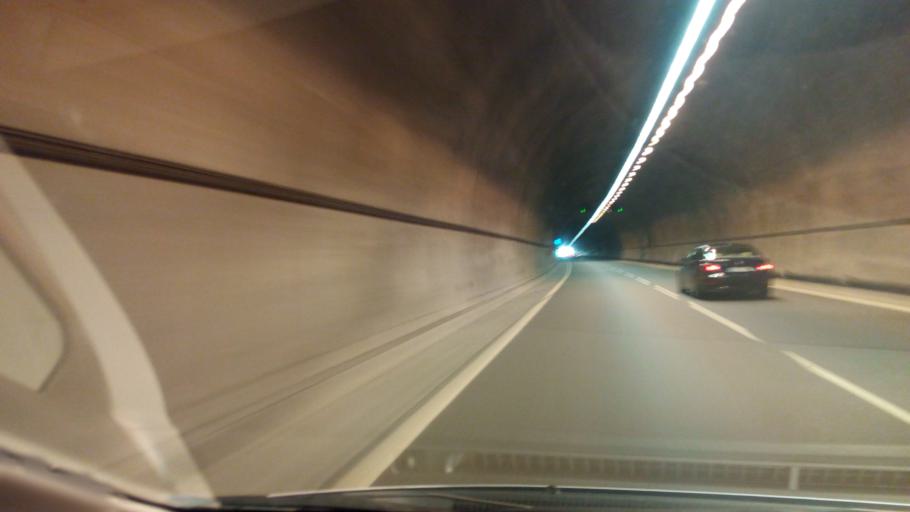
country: CY
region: Limassol
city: Sotira
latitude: 34.6969
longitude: 32.8355
